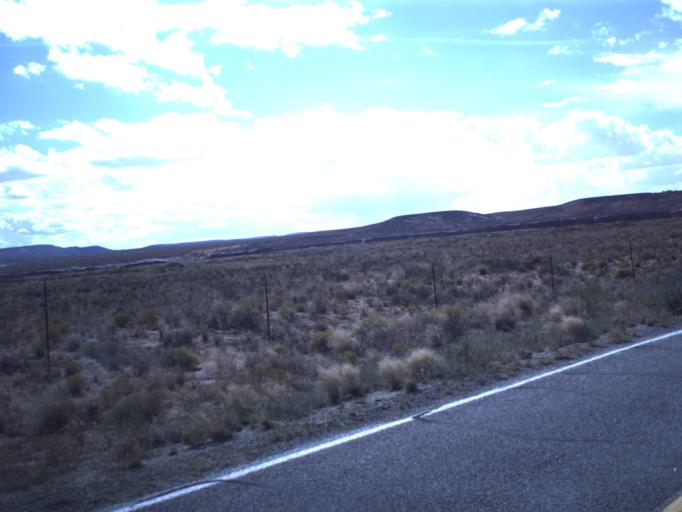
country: US
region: Utah
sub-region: San Juan County
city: Blanding
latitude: 37.2875
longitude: -109.4908
